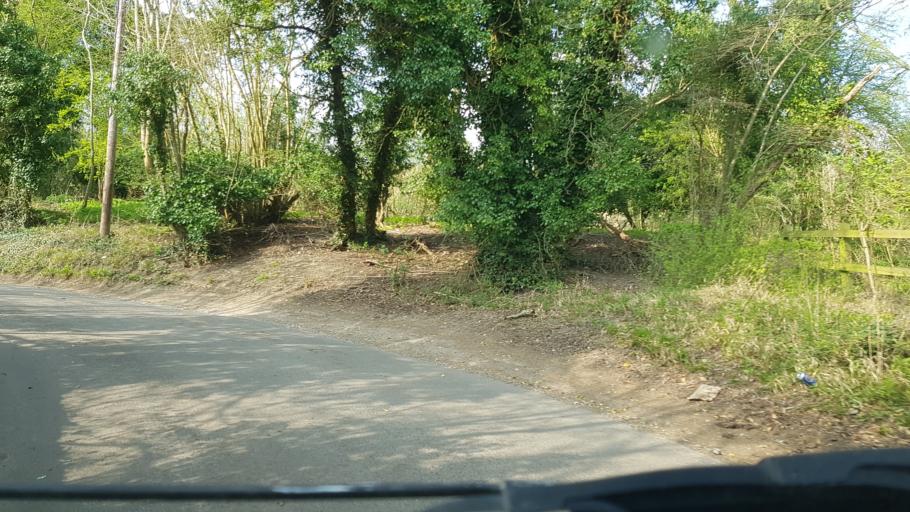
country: GB
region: England
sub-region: Surrey
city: Chilworth
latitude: 51.2300
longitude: -0.5206
